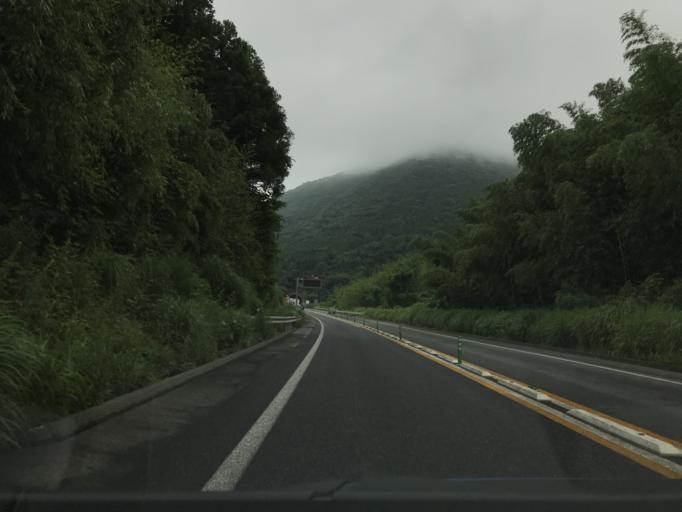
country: JP
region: Oita
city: Bungo-Takada-shi
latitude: 33.4915
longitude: 131.3216
